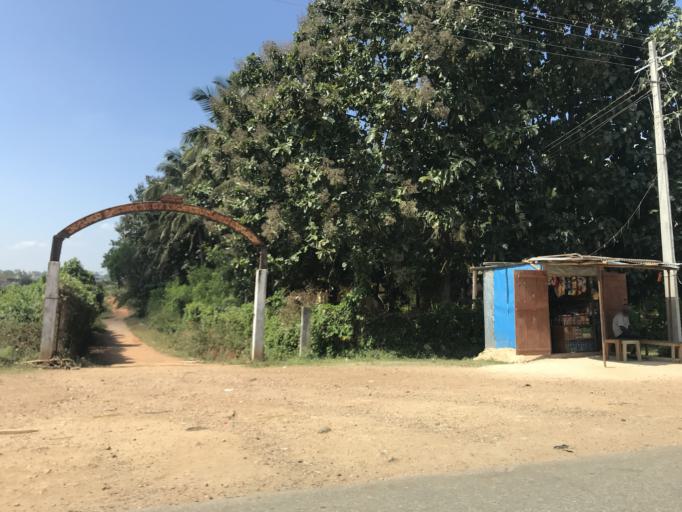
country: IN
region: Karnataka
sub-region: Mysore
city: Heggadadevankote
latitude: 12.0942
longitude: 76.3317
